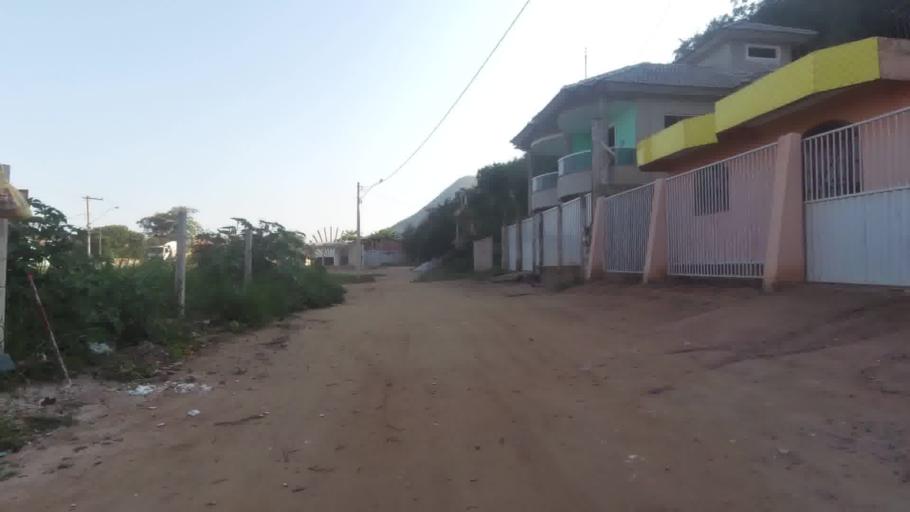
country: BR
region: Espirito Santo
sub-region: Piuma
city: Piuma
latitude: -20.8571
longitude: -40.7547
